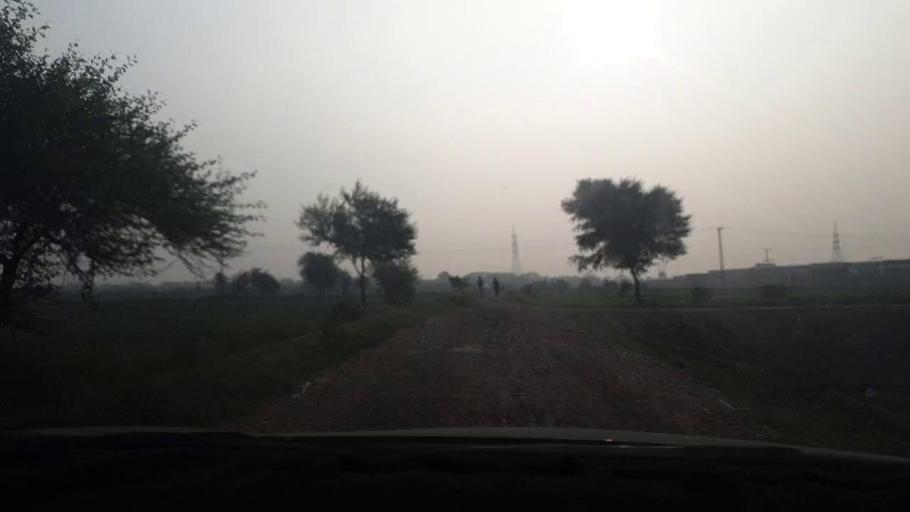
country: PK
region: Sindh
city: Matiari
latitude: 25.5813
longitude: 68.4600
